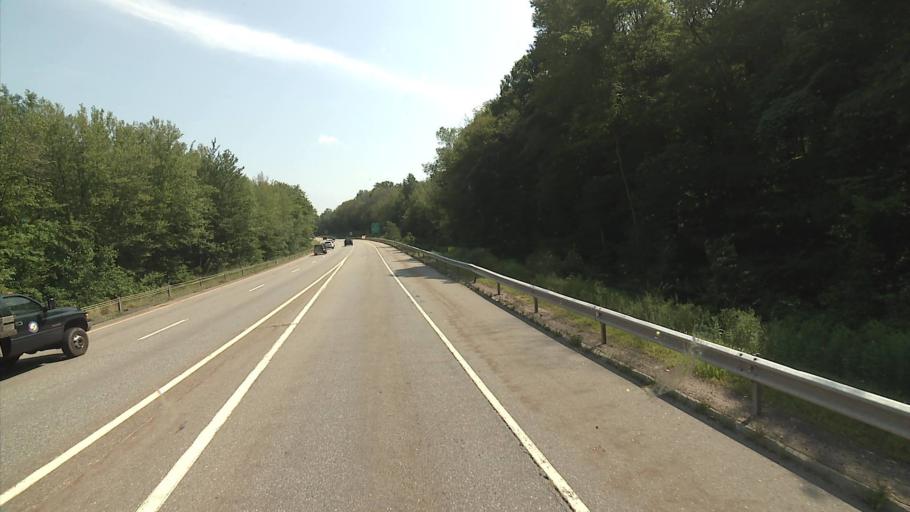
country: US
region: Connecticut
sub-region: Middlesex County
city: Chester Center
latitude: 41.4134
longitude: -72.4871
